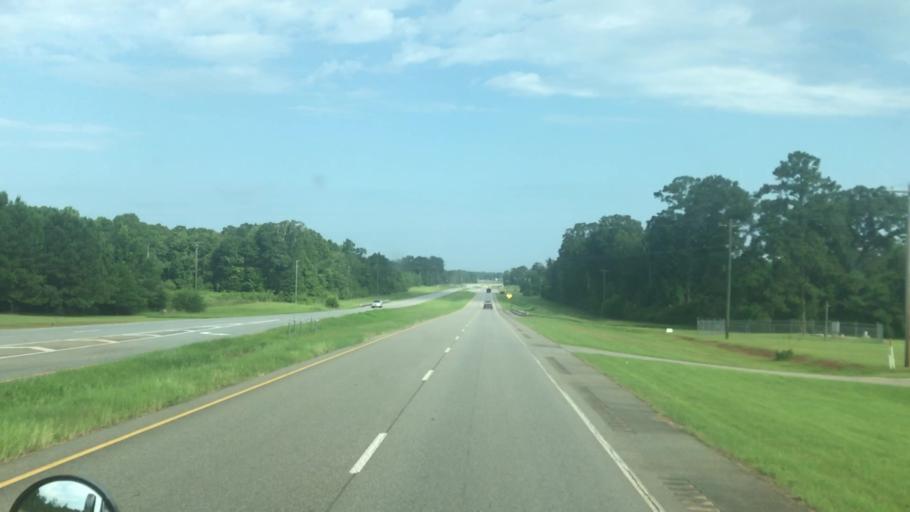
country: US
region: Georgia
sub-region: Early County
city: Blakely
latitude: 31.3460
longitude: -84.9113
